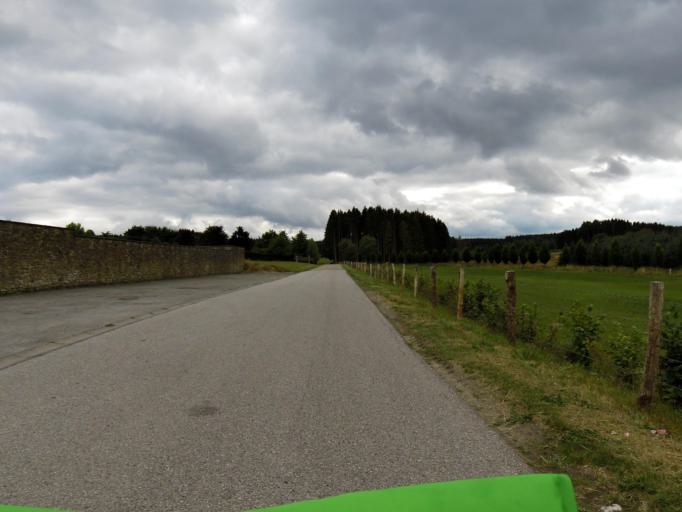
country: BE
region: Wallonia
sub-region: Province de Namur
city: Bievre
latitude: 49.9354
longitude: 5.0180
